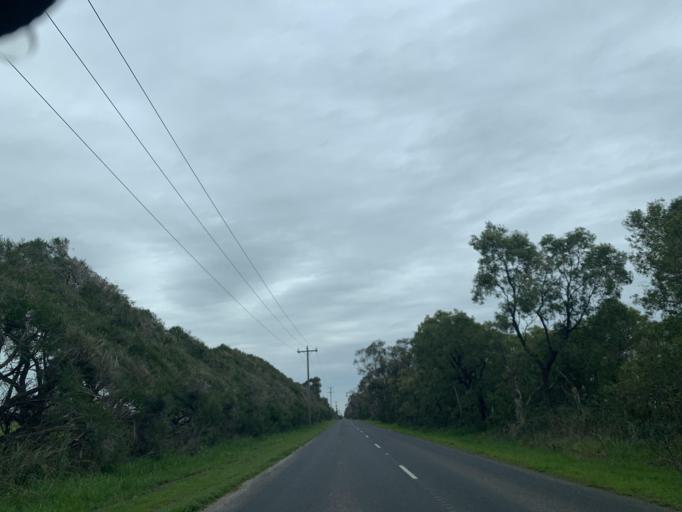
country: AU
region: Victoria
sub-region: Cardinia
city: Garfield
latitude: -38.0839
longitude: 145.6058
